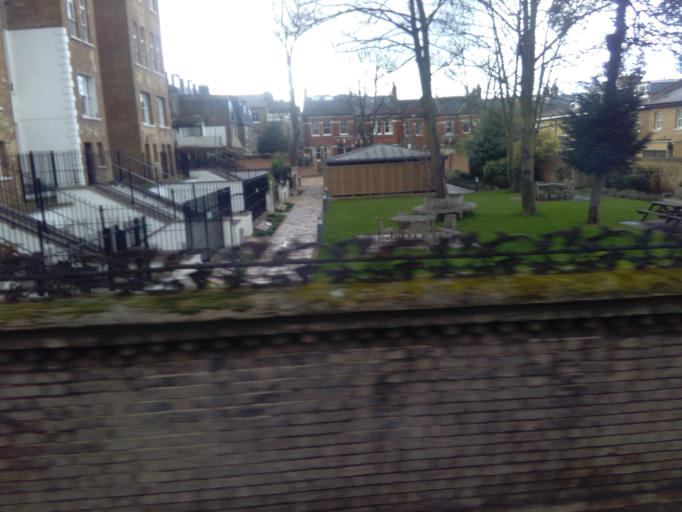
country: GB
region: England
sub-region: Greater London
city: Battersea
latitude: 51.4617
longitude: -0.1491
